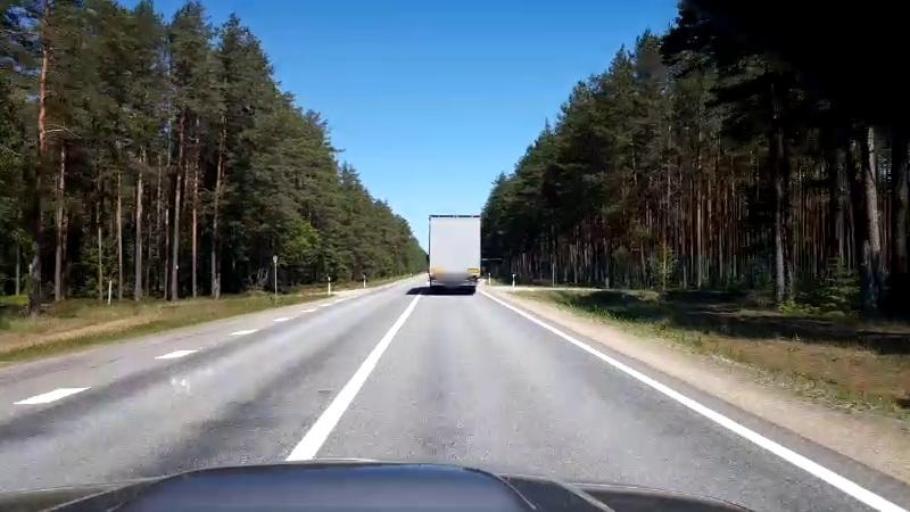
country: LV
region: Salacgrivas
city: Salacgriva
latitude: 57.5419
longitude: 24.4320
